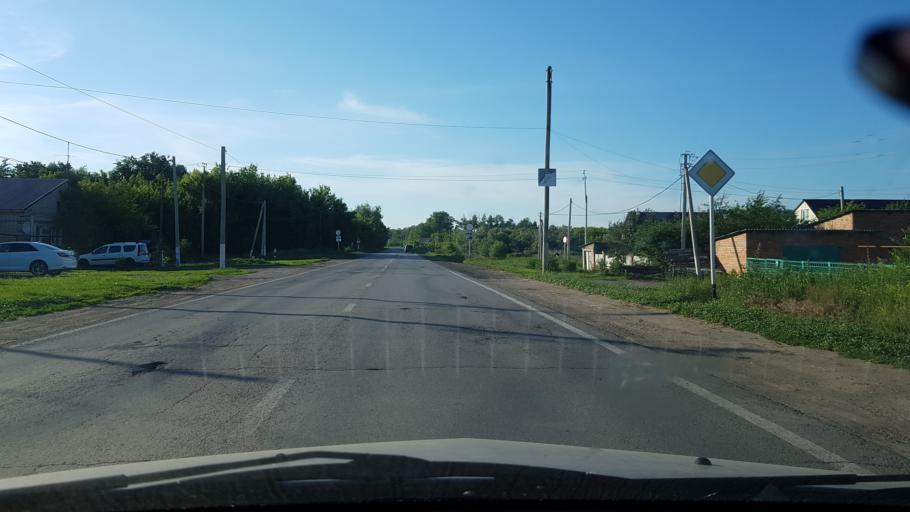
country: RU
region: Samara
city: Tol'yatti
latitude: 53.6508
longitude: 49.2916
